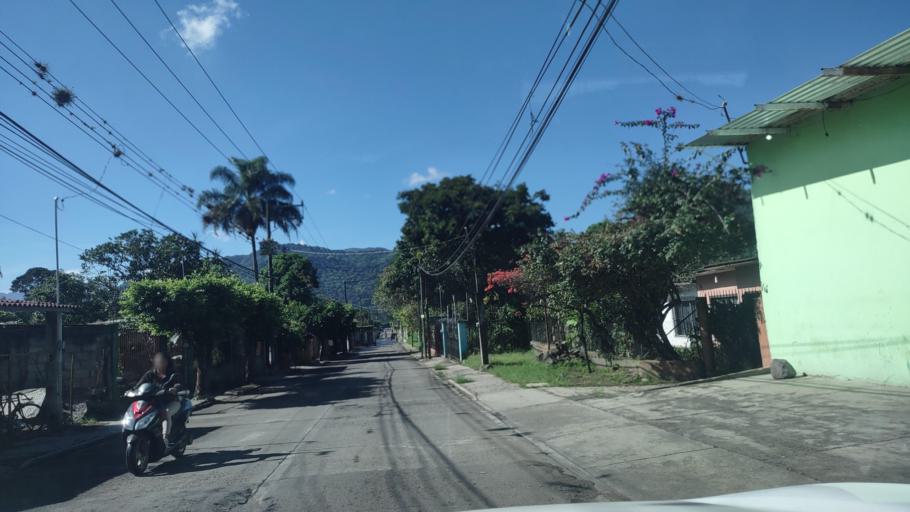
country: MX
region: Veracruz
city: Cuautlapan
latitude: 18.8711
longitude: -97.0230
